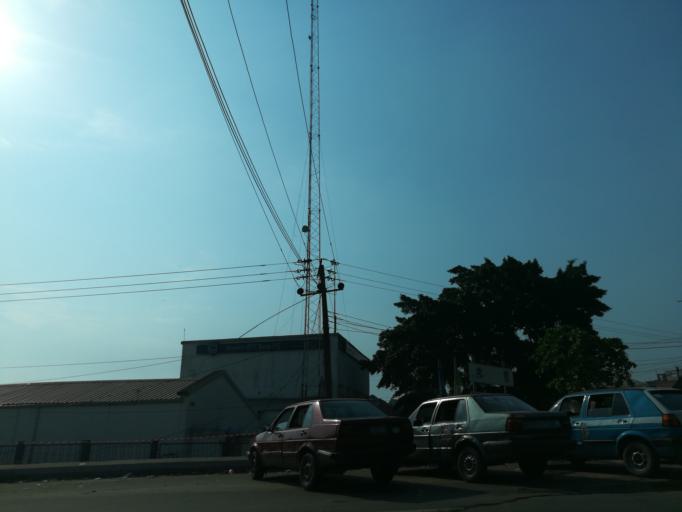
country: NG
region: Rivers
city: Port Harcourt
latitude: 4.8059
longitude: 7.0107
